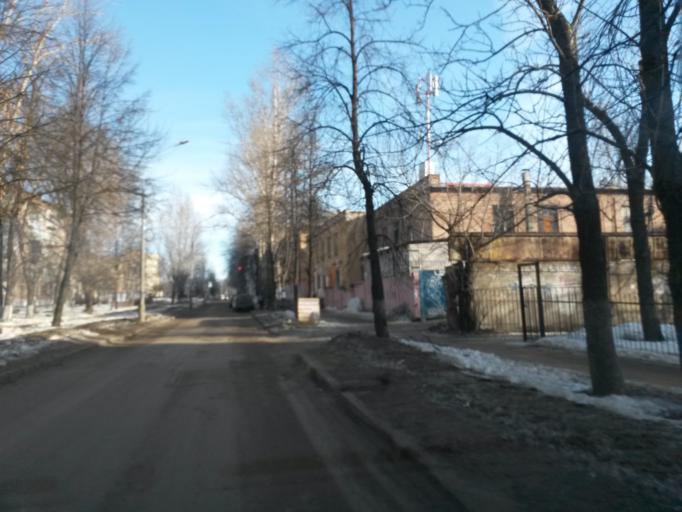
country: RU
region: Jaroslavl
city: Yaroslavl
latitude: 57.6238
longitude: 39.8533
